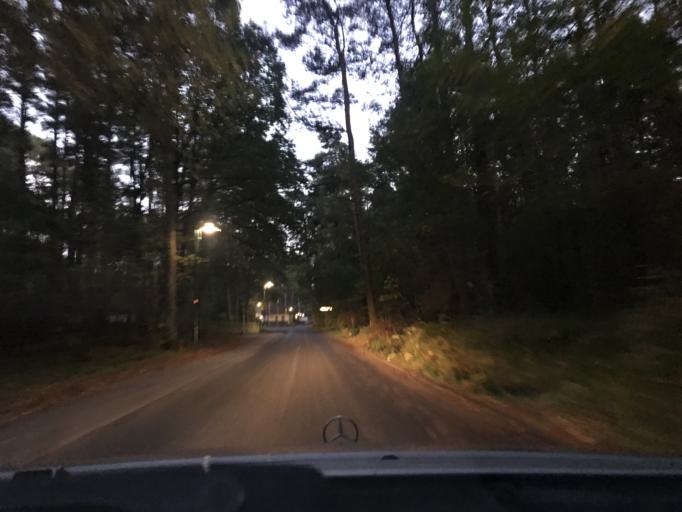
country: DE
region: Mecklenburg-Vorpommern
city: Karlshagen
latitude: 54.1192
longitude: 13.8429
